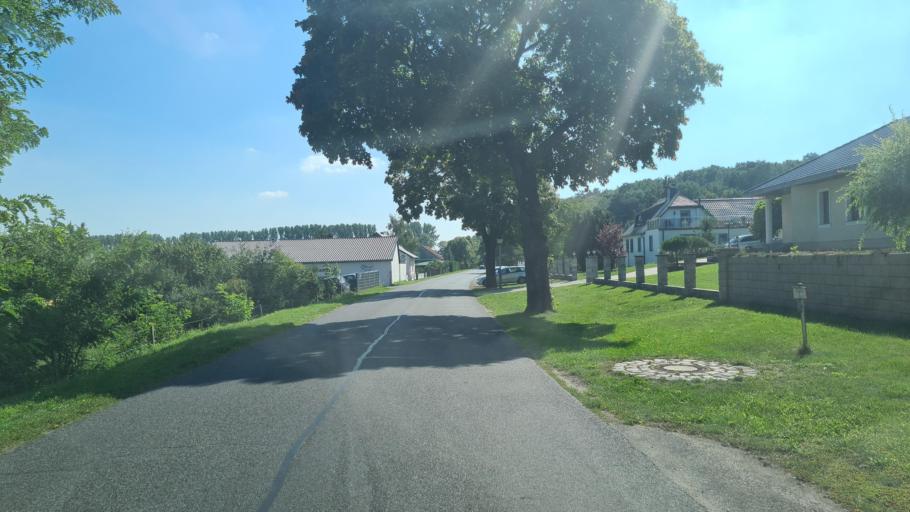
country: DE
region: Brandenburg
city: Friesack
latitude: 52.7095
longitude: 12.6438
